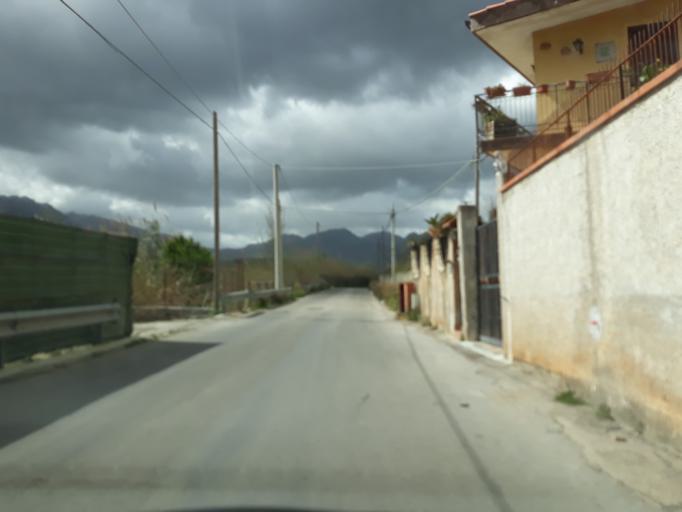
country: IT
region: Sicily
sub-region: Palermo
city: Monreale
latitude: 38.0788
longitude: 13.2928
